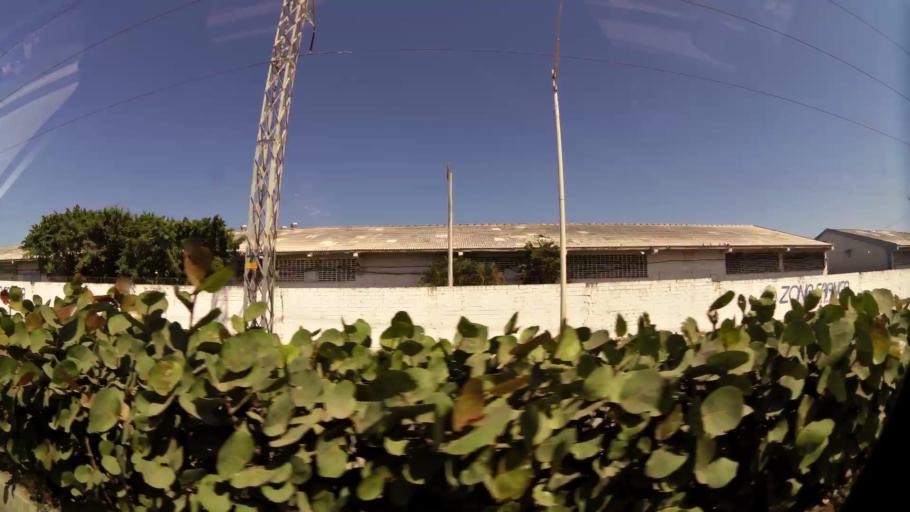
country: CO
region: Atlantico
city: Barranquilla
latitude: 10.9621
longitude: -74.7683
